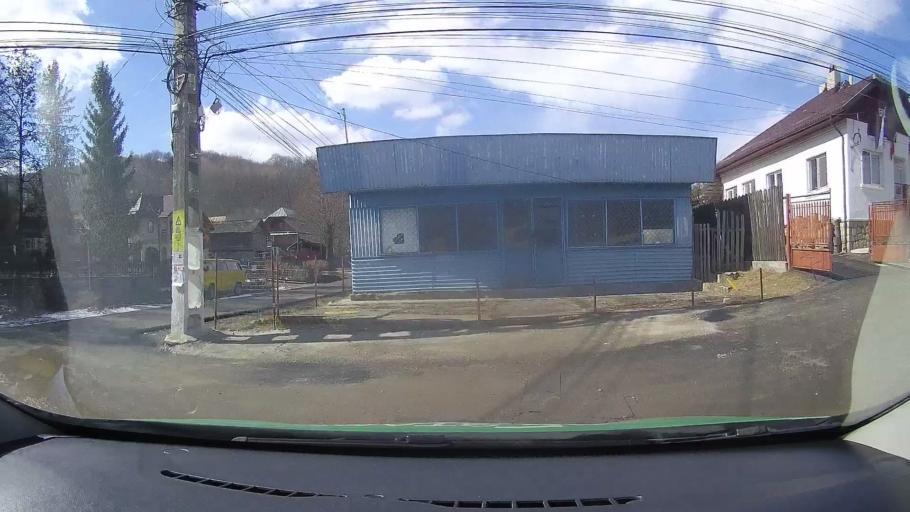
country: RO
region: Dambovita
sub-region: Comuna Runcu
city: Runcu
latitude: 45.1740
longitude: 25.3885
